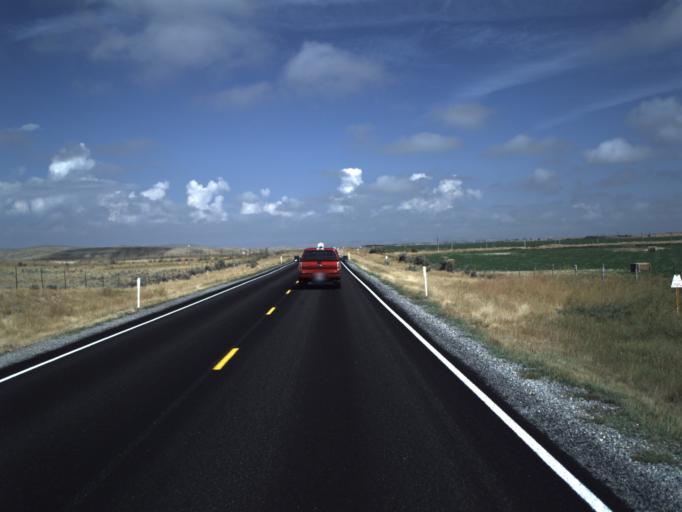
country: US
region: Utah
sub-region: Rich County
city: Randolph
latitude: 41.5598
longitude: -111.1567
